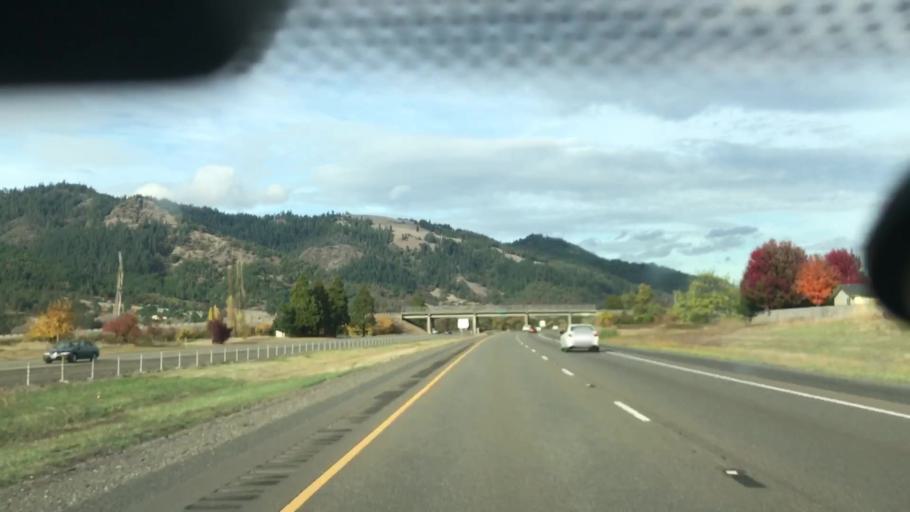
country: US
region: Oregon
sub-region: Douglas County
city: Tri-City
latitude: 42.9831
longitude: -123.3319
